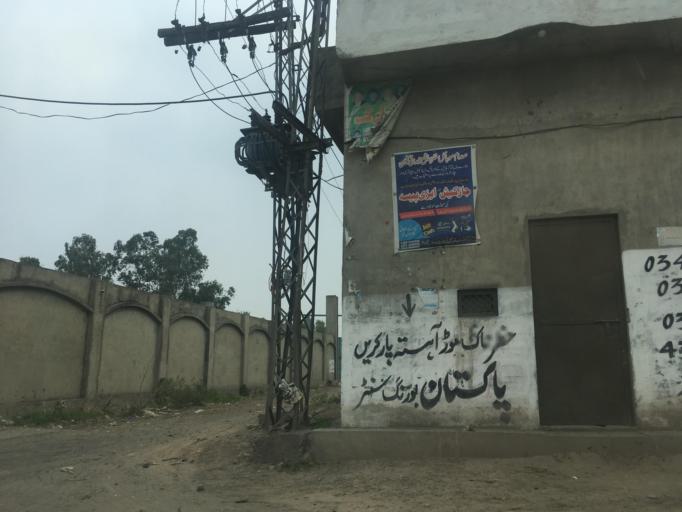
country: PK
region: Punjab
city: Lahore
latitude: 31.6180
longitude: 74.3682
